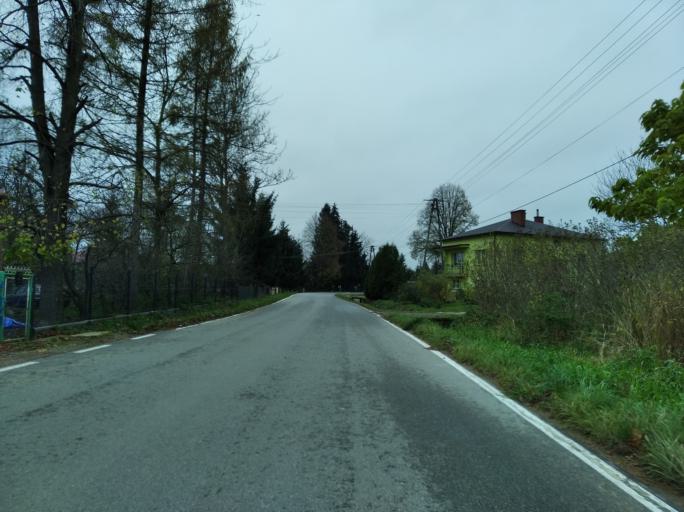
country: PL
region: Subcarpathian Voivodeship
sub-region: Powiat krosnienski
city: Leki
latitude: 49.8088
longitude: 21.6592
